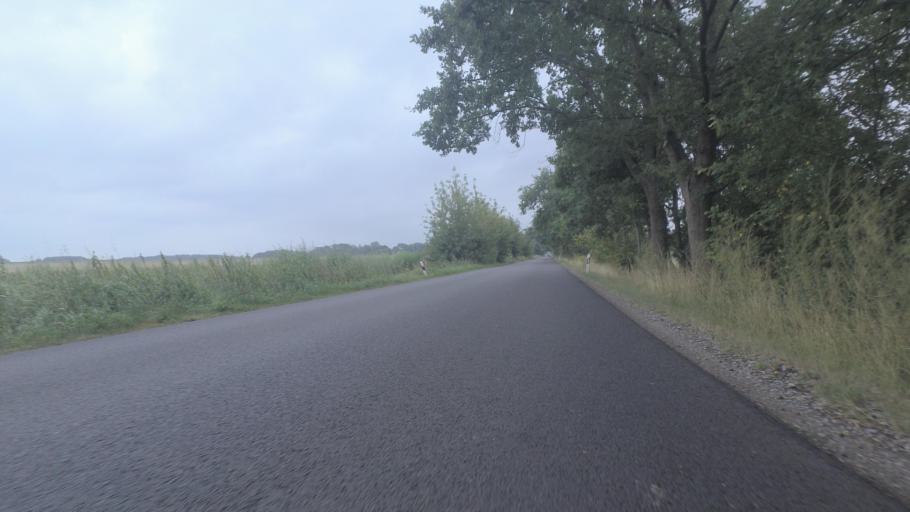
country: DE
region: Brandenburg
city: Wustermark
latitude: 52.4818
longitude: 12.9899
